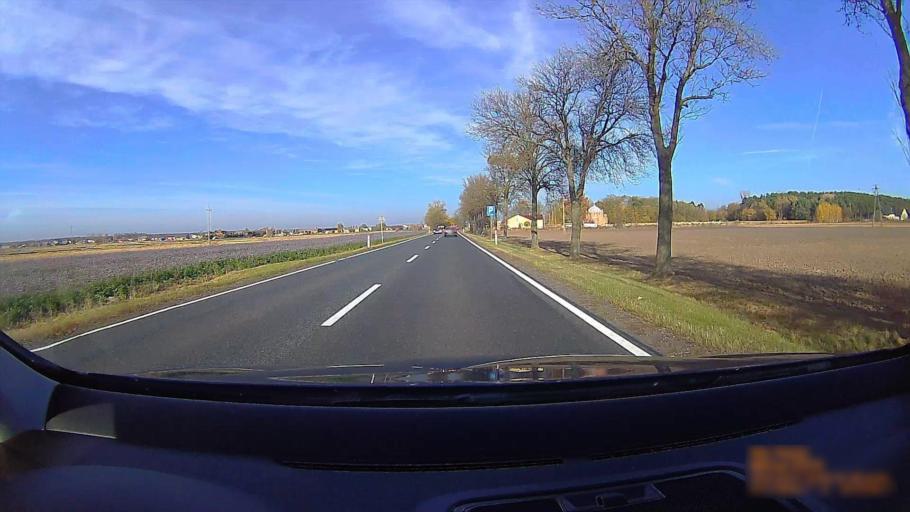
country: PL
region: Greater Poland Voivodeship
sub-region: Powiat kaliski
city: Stawiszyn
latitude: 51.9462
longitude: 18.1292
